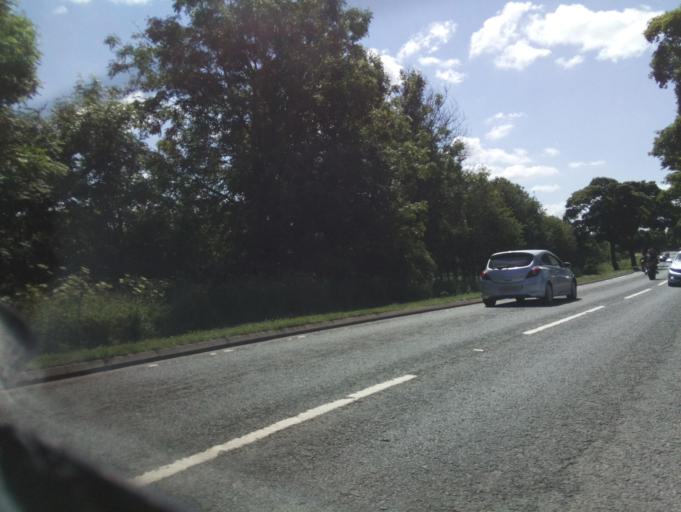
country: GB
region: England
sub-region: Derbyshire
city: Buxton
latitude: 53.2676
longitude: -1.8976
